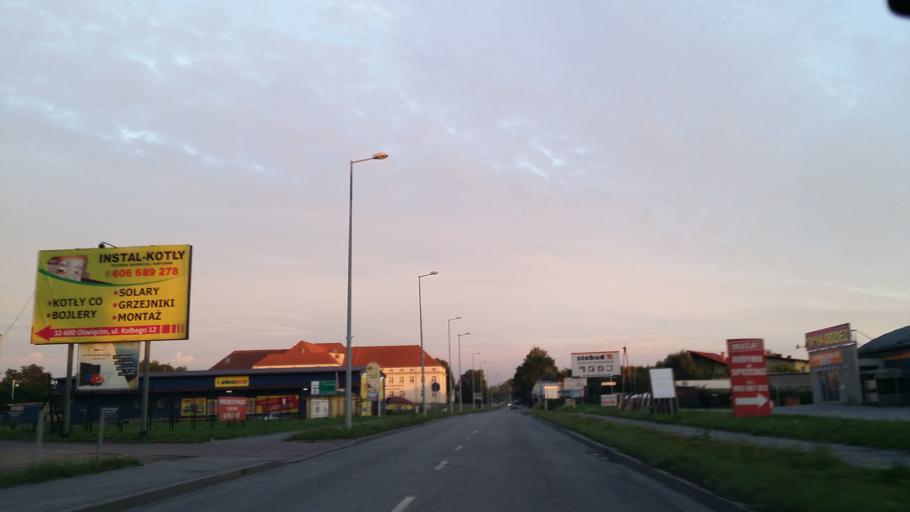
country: PL
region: Lesser Poland Voivodeship
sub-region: Powiat oswiecimski
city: Brzezinka
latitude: 50.0287
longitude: 19.1960
